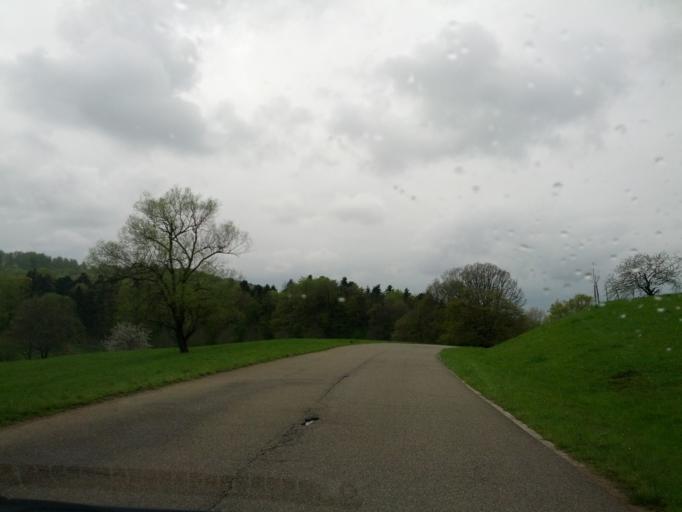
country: DE
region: Baden-Wuerttemberg
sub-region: Freiburg Region
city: Wittnau
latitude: 47.9446
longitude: 7.7953
